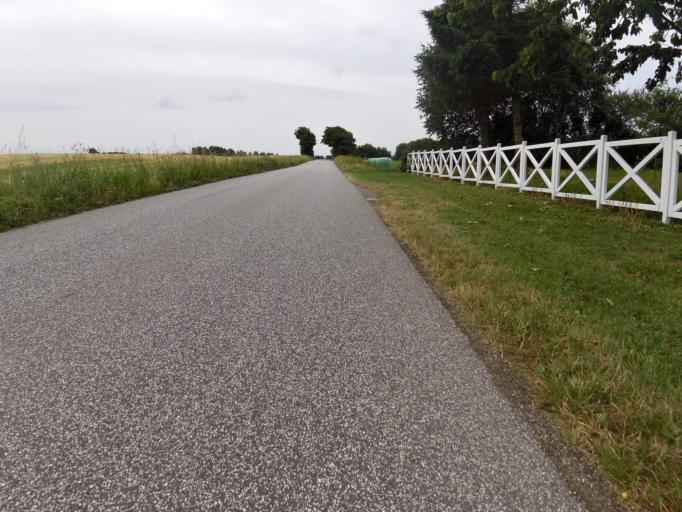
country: DK
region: Central Jutland
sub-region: Holstebro Kommune
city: Holstebro
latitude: 56.4126
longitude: 8.6707
